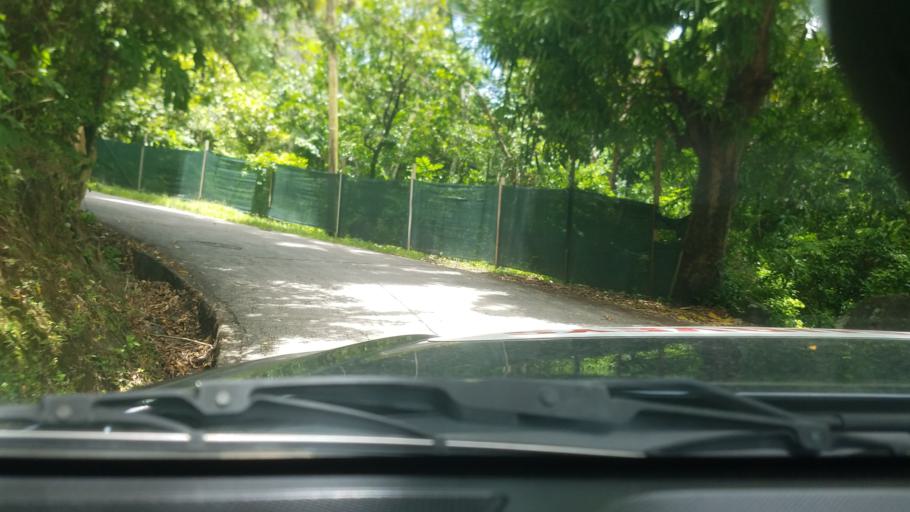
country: LC
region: Soufriere
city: Soufriere
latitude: 13.8396
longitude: -61.0615
